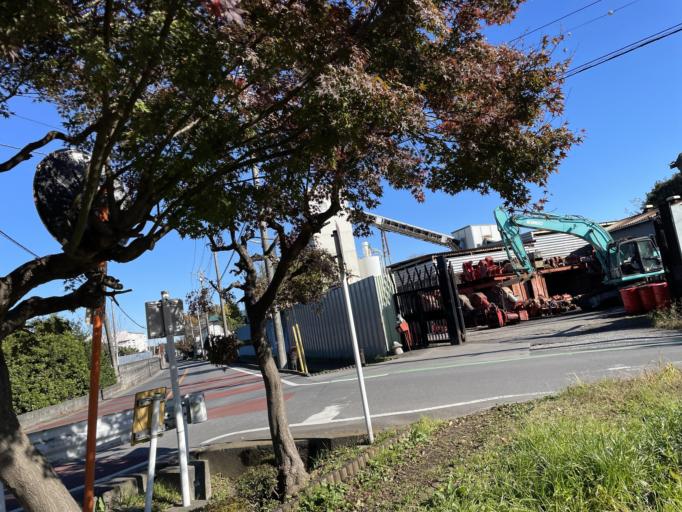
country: JP
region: Tokyo
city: Tanashicho
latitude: 35.7795
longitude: 139.5520
